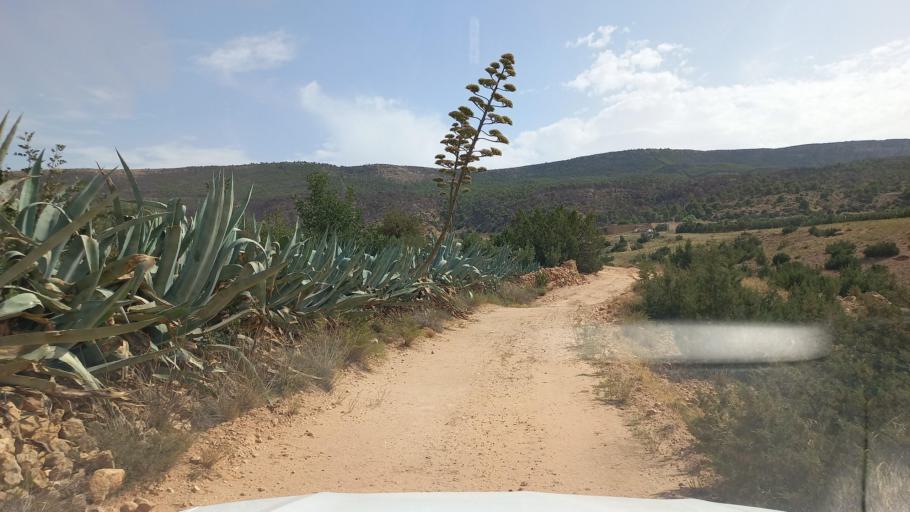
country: TN
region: Al Qasrayn
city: Kasserine
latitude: 35.3578
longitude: 8.8881
